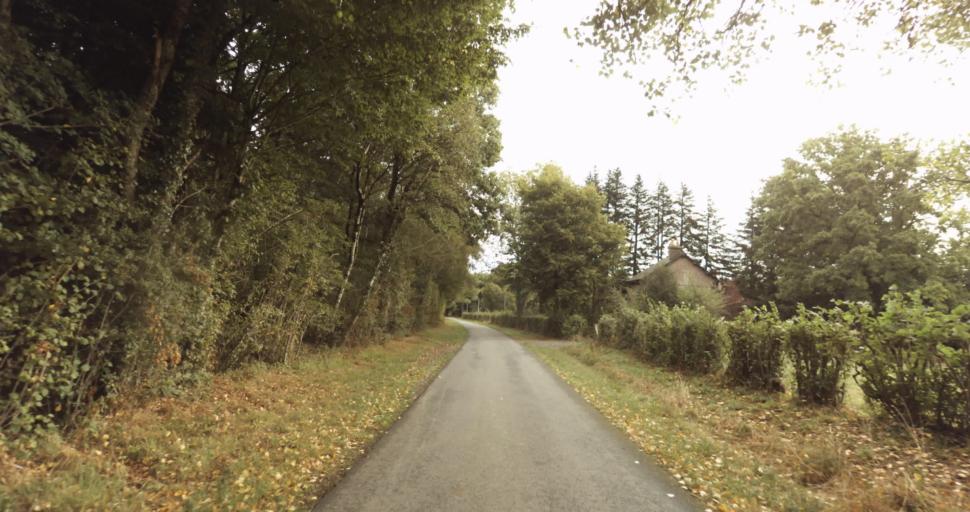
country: FR
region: Lower Normandy
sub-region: Departement de l'Orne
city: Gace
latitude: 48.8748
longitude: 0.3092
